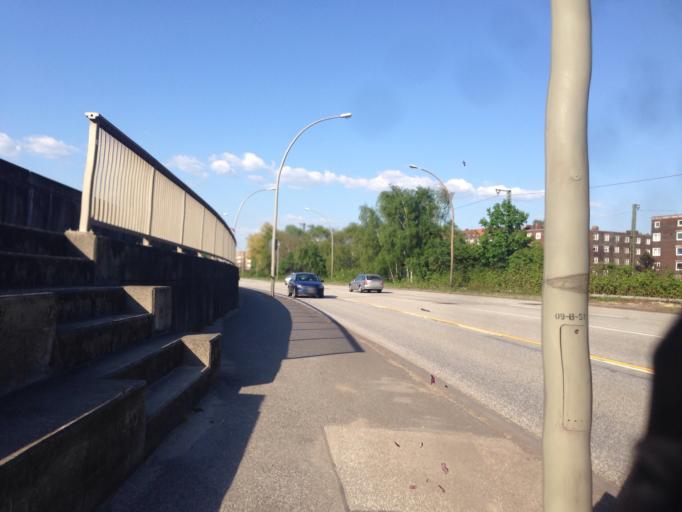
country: DE
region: Hamburg
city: Kleiner Grasbrook
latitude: 53.5238
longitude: 10.0132
